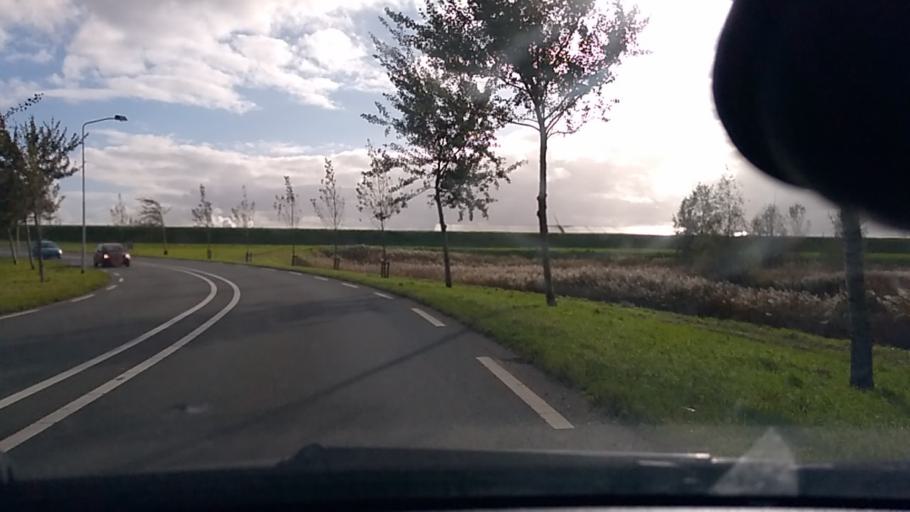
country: NL
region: North Holland
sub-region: Gemeente Zaanstad
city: Zaanstad
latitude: 52.4272
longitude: 4.7881
